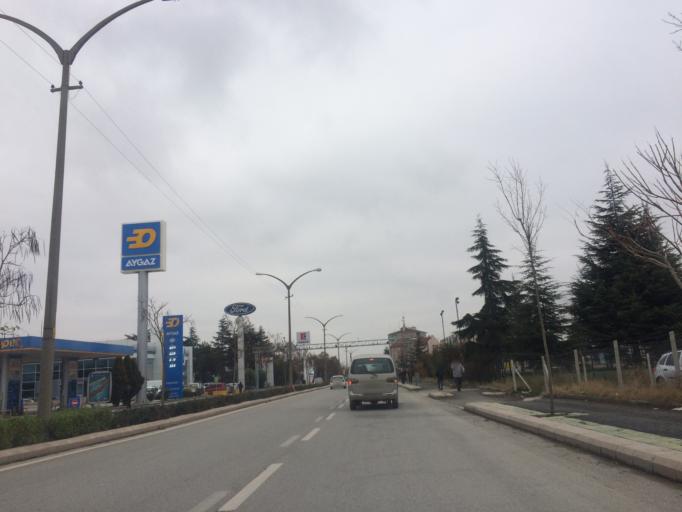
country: TR
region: Eskisehir
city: Eskisehir
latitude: 39.7904
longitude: 30.4797
